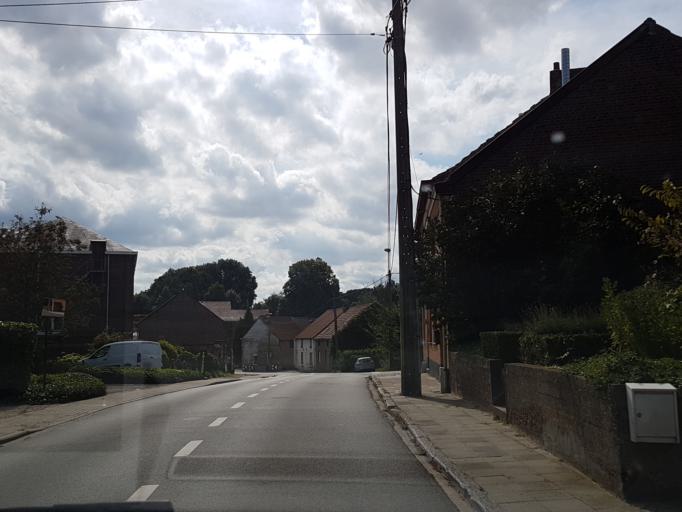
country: BE
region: Flanders
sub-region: Provincie Vlaams-Brabant
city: Bertem
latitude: 50.8425
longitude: 4.6407
